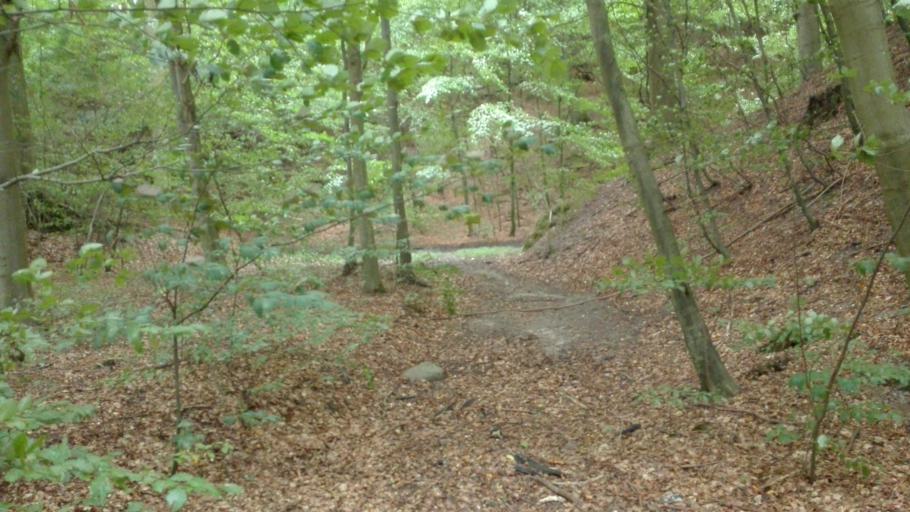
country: DK
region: Central Jutland
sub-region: Arhus Kommune
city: Beder
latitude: 56.1023
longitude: 10.2367
